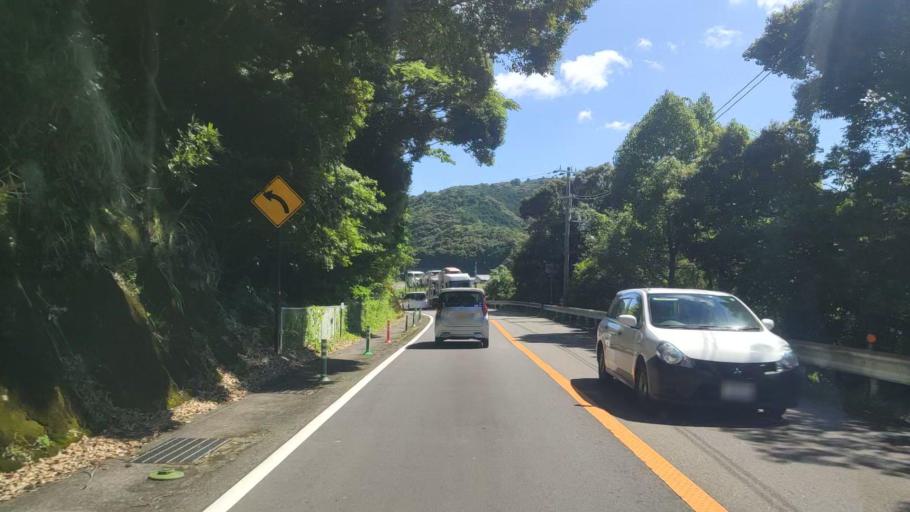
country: JP
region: Wakayama
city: Shingu
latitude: 33.5864
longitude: 135.9185
